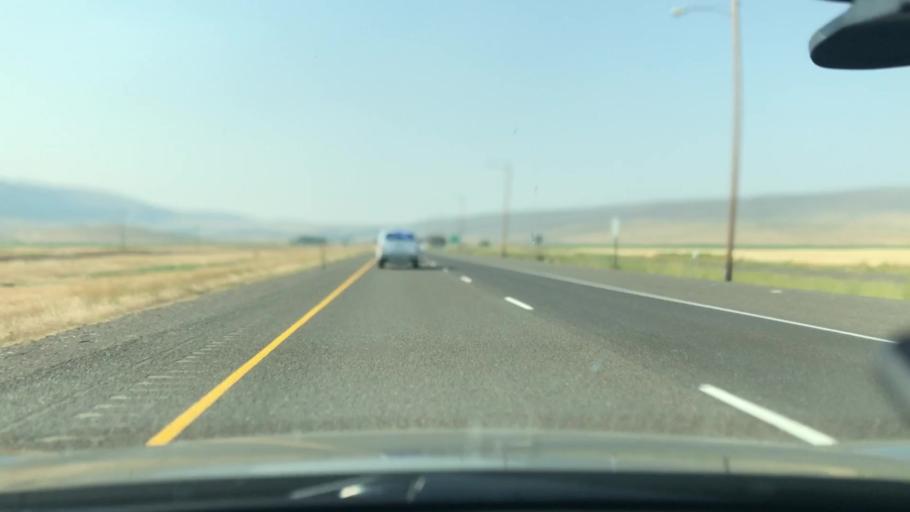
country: US
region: Oregon
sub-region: Union County
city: Union
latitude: 45.1054
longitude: -117.9561
